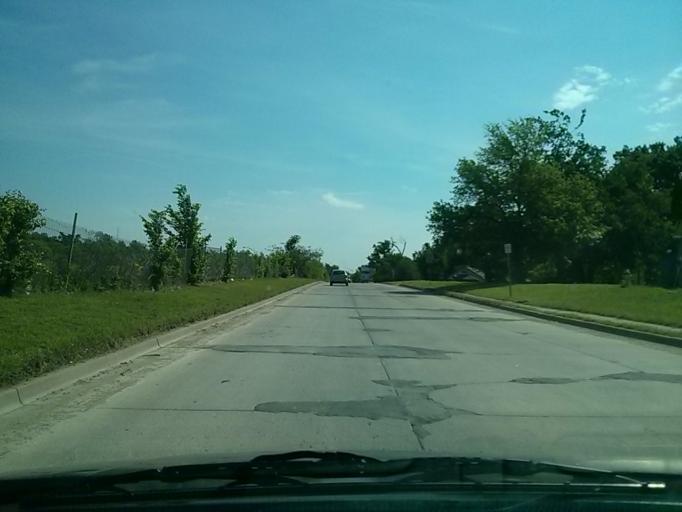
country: US
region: Oklahoma
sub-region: Tulsa County
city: Tulsa
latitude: 36.1588
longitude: -95.9662
